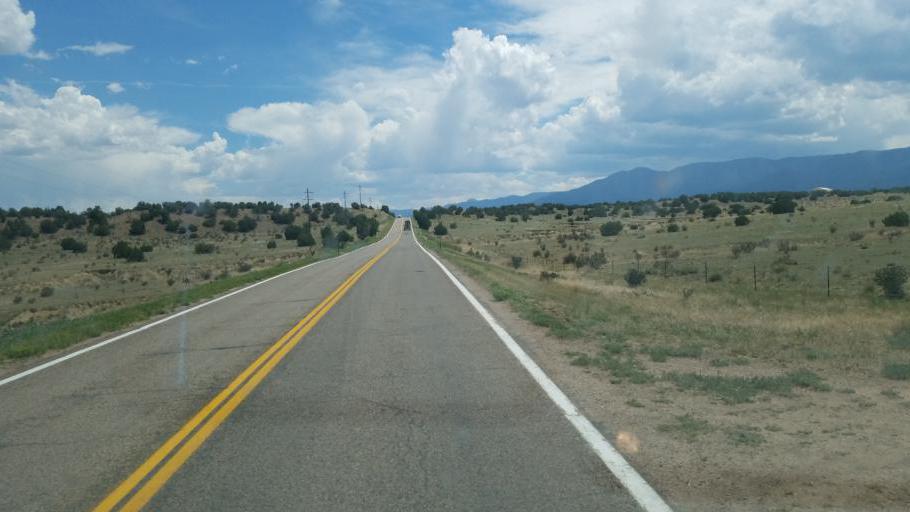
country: US
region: Colorado
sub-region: Fremont County
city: Florence
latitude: 38.3346
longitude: -105.1058
